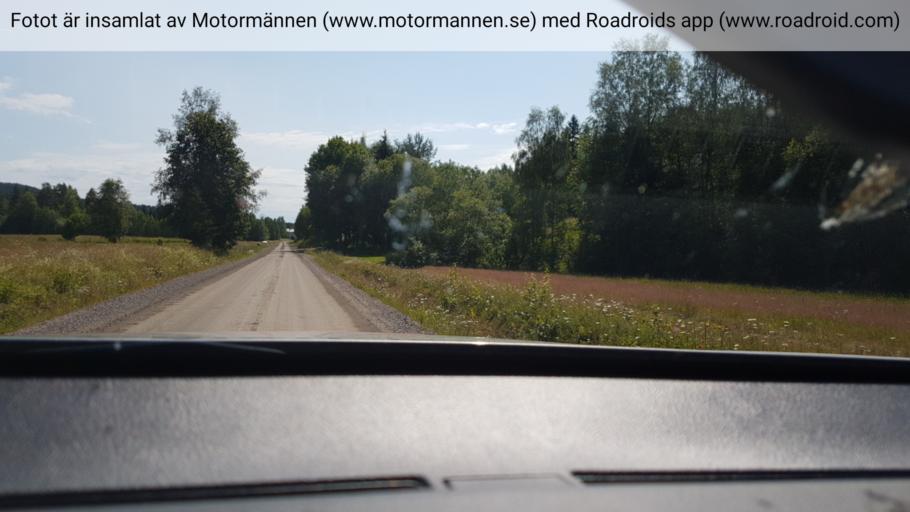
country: SE
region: Vaermland
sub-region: Torsby Kommun
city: Torsby
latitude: 60.5062
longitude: 13.1507
